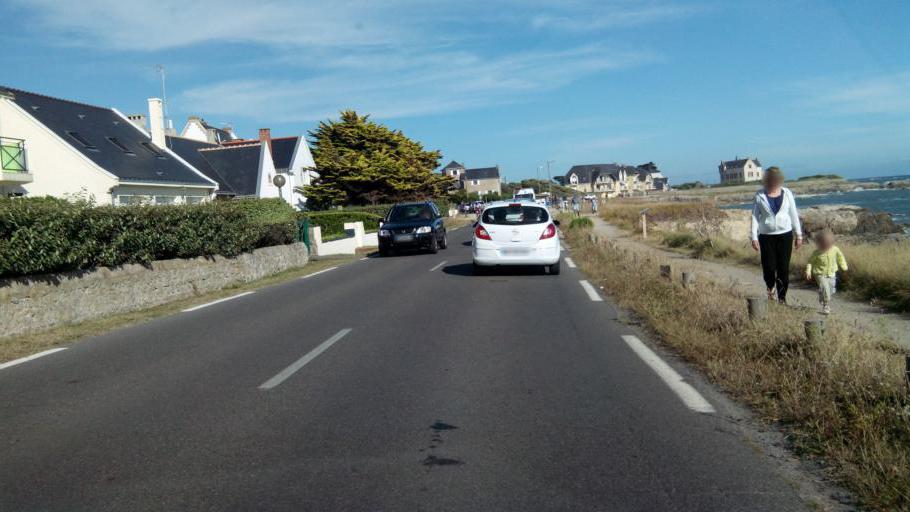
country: FR
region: Pays de la Loire
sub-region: Departement de la Loire-Atlantique
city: Le Croisic
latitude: 47.2824
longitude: -2.5094
